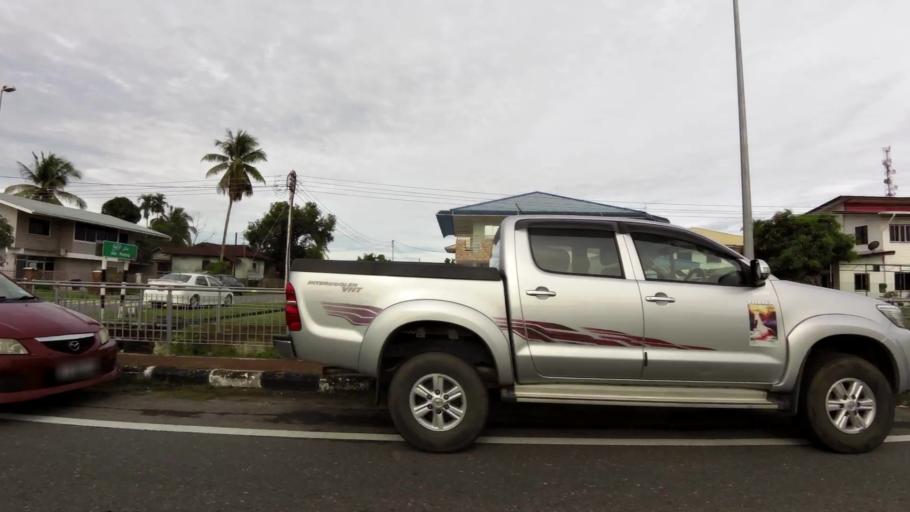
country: BN
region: Belait
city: Seria
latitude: 4.6122
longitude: 114.3351
